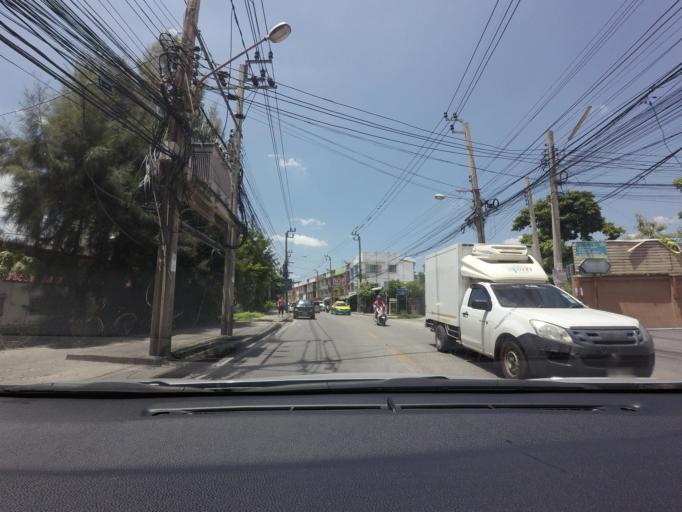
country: TH
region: Bangkok
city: Suan Luang
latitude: 13.7062
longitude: 100.6348
